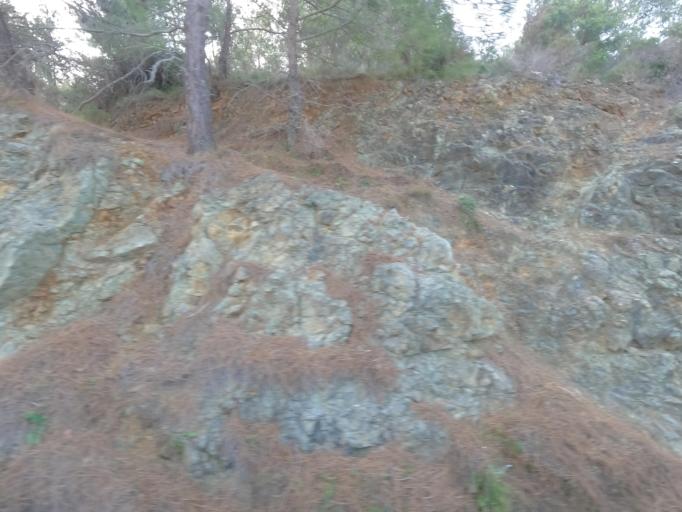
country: CY
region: Pafos
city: Polis
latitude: 35.0011
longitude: 32.3394
